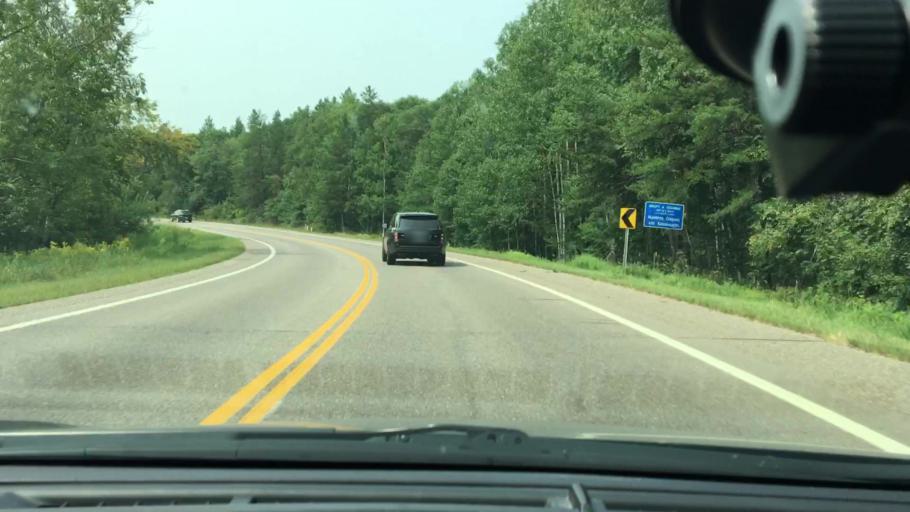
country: US
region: Minnesota
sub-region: Cass County
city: East Gull Lake
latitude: 46.3828
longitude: -94.3299
